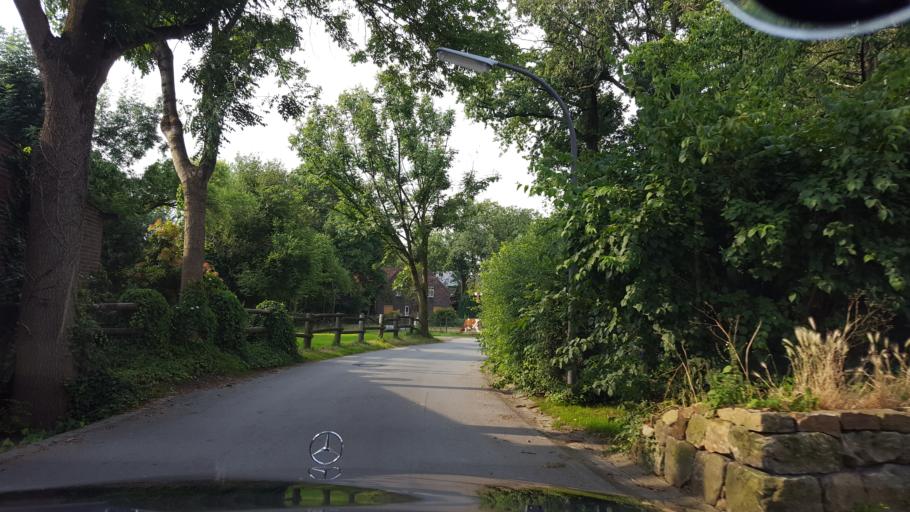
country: DE
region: North Rhine-Westphalia
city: Oer-Erkenschwick
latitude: 51.6221
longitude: 7.2539
